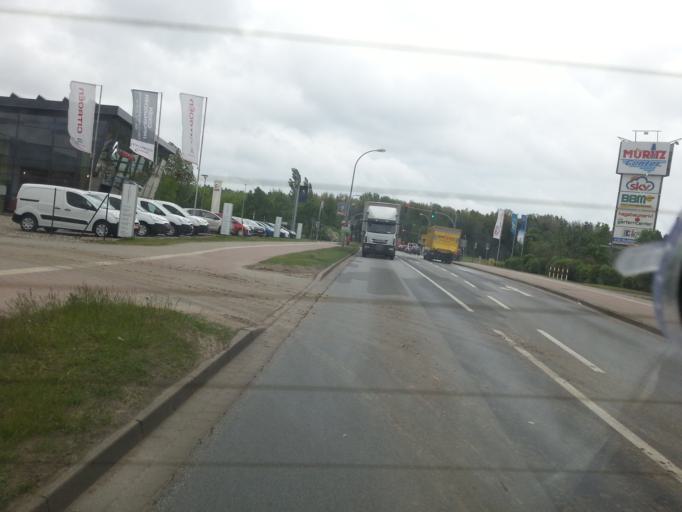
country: DE
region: Mecklenburg-Vorpommern
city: Waren
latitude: 53.5208
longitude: 12.6504
